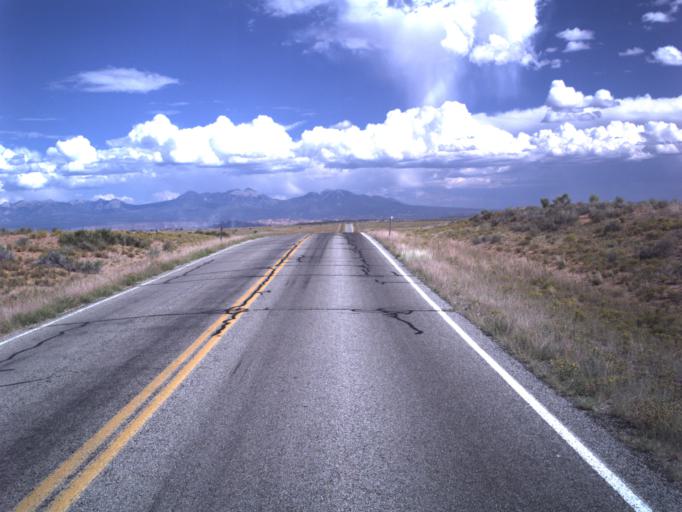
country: US
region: Utah
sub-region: Grand County
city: Moab
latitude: 38.5512
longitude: -109.7851
